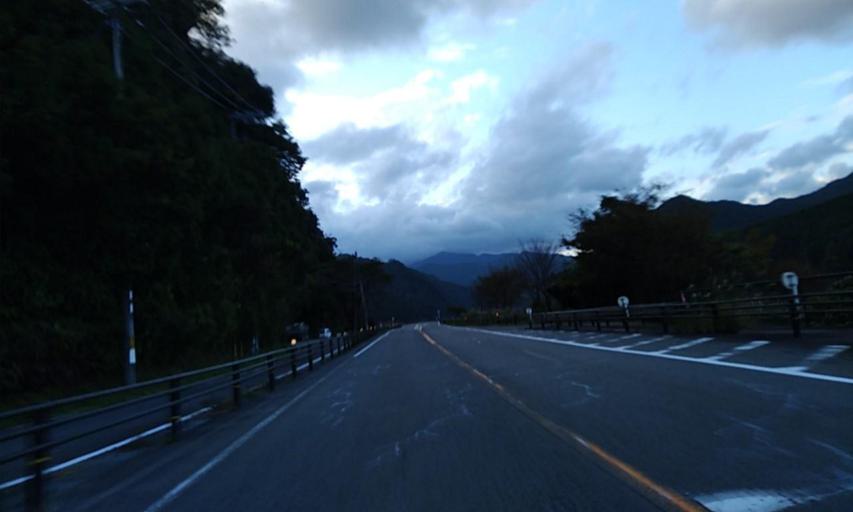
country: JP
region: Wakayama
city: Shingu
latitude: 33.7239
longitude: 135.9624
